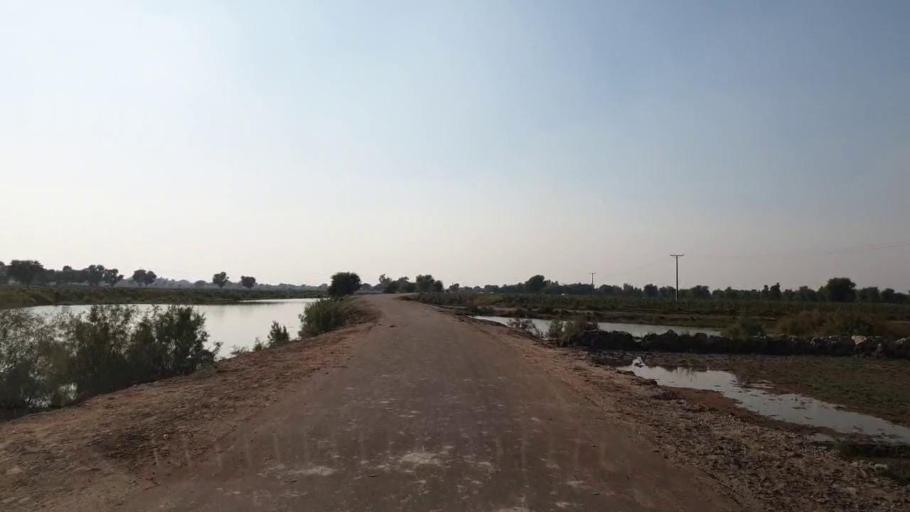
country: PK
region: Sindh
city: Sehwan
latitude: 26.4377
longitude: 67.7962
